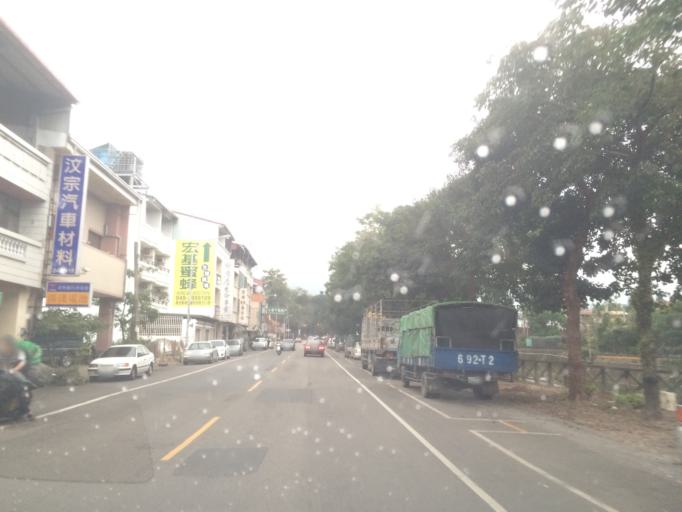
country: TW
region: Taiwan
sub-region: Nantou
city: Puli
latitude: 23.9589
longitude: 120.9653
